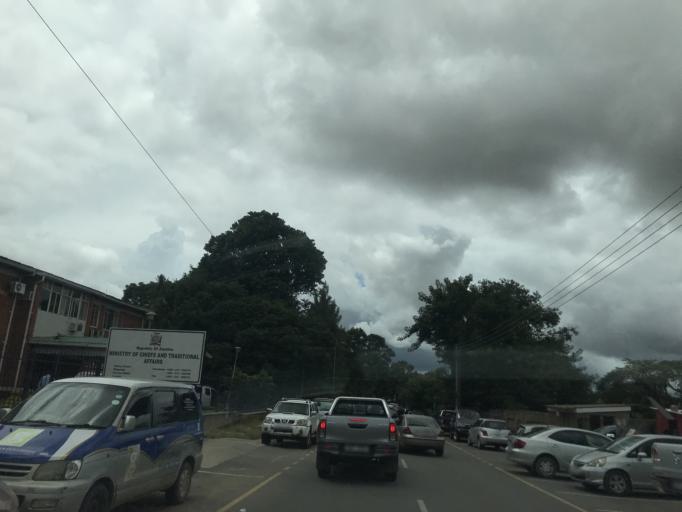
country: ZM
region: Lusaka
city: Lusaka
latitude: -15.4245
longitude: 28.3080
